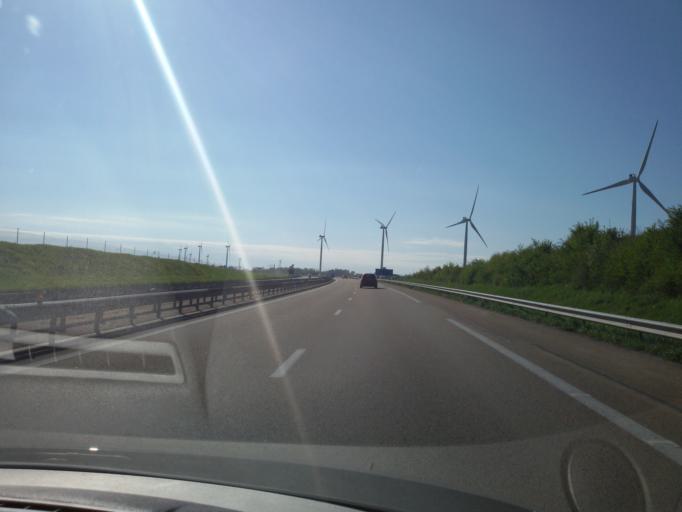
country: FR
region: Bourgogne
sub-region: Departement de l'Yonne
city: Venoy
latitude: 47.7835
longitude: 3.6784
